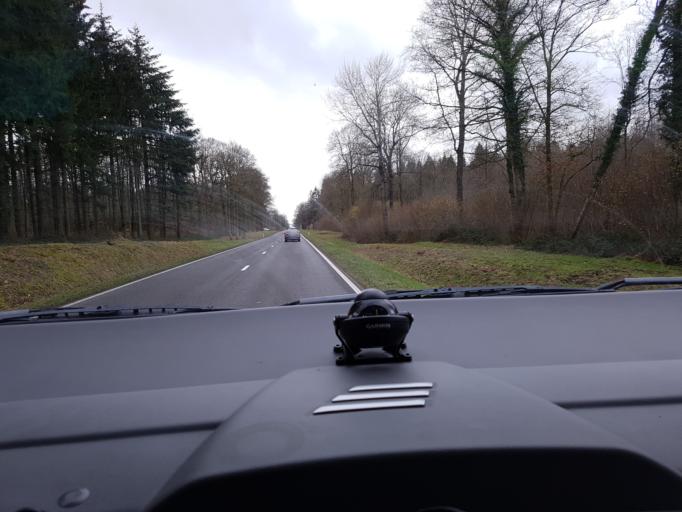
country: BE
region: Wallonia
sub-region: Province de Namur
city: Florennes
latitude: 50.2154
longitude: 4.6188
